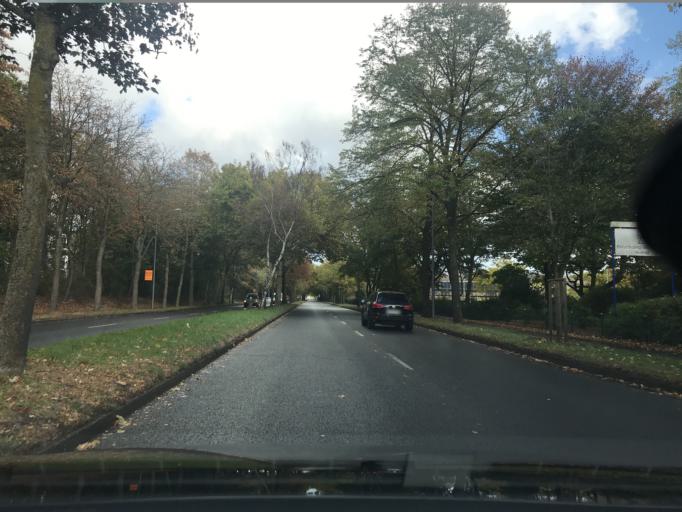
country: DE
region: North Rhine-Westphalia
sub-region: Regierungsbezirk Dusseldorf
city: Krefeld
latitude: 51.3387
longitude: 6.6098
